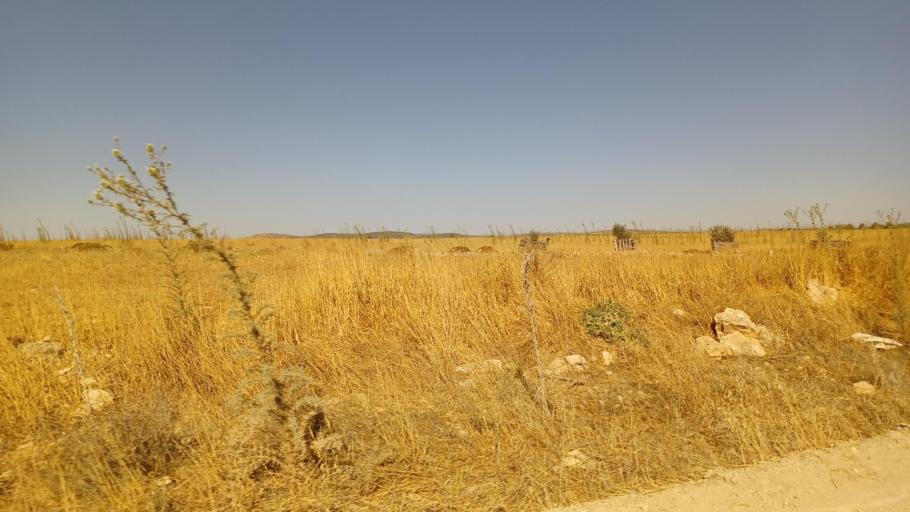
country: CY
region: Larnaka
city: Pergamos
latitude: 35.0502
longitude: 33.7020
